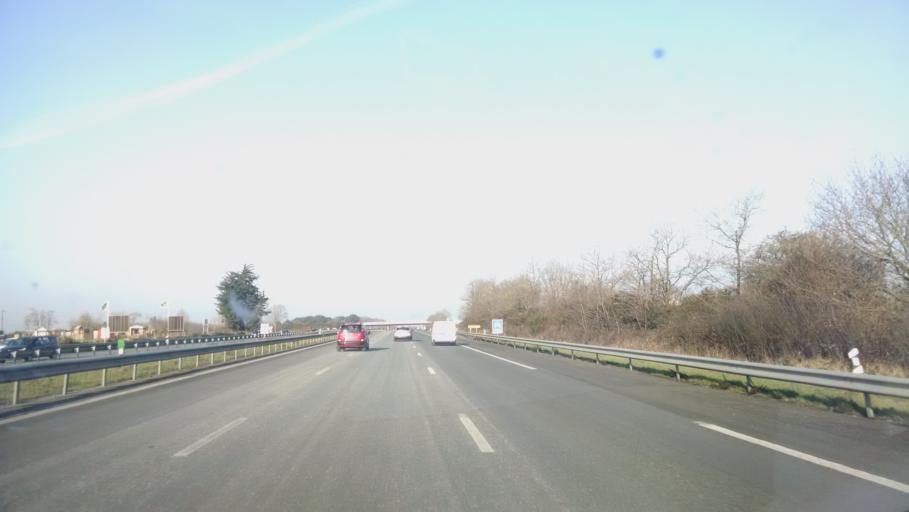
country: FR
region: Pays de la Loire
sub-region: Departement de la Loire-Atlantique
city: Malville
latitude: 47.3534
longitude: -1.8864
